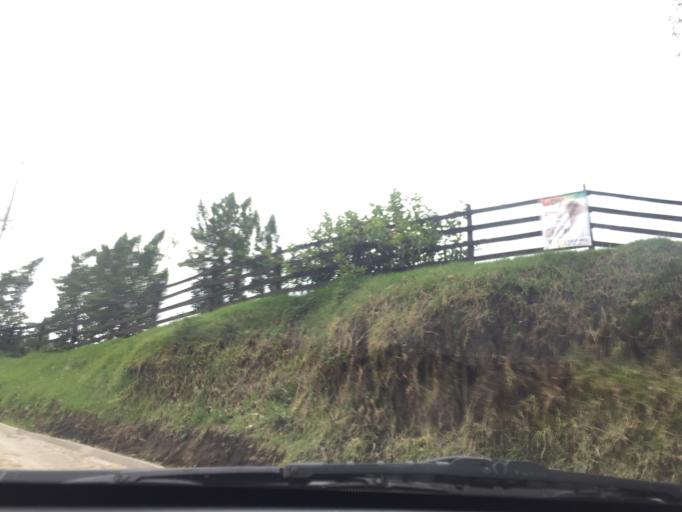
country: CO
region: Cundinamarca
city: Tabio
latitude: 4.9348
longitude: -74.1287
